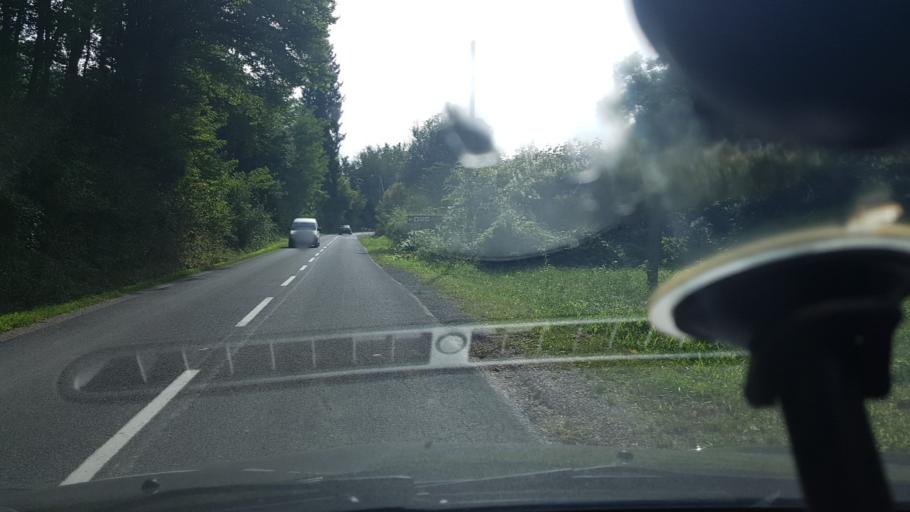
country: HR
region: Varazdinska
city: Remetinec
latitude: 46.1100
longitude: 16.2151
